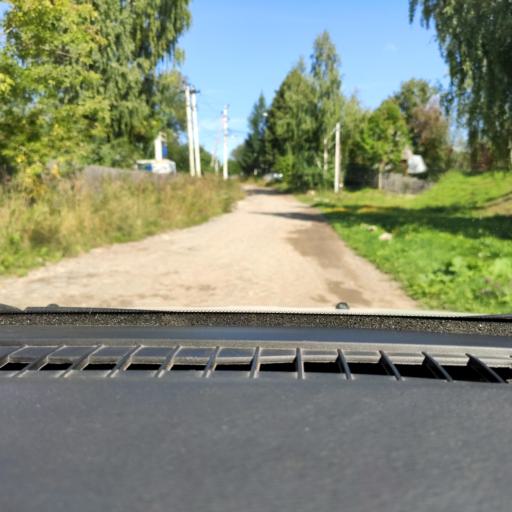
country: RU
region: Perm
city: Perm
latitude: 58.1152
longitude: 56.3926
